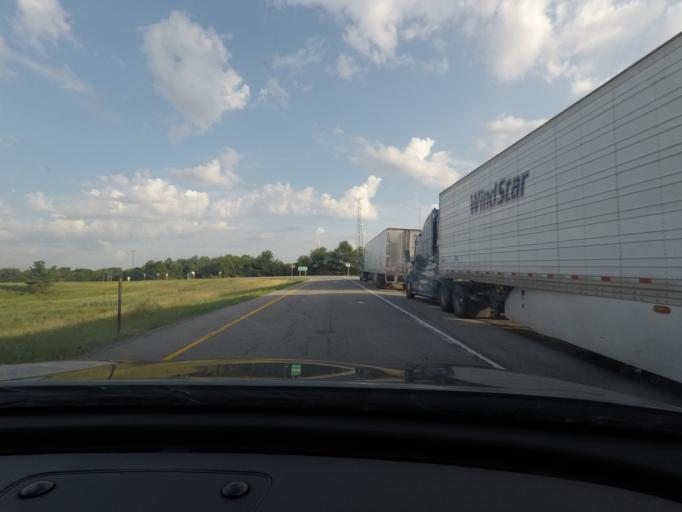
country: US
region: Illinois
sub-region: Jefferson County
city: Mount Vernon
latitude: 38.3630
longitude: -89.0326
